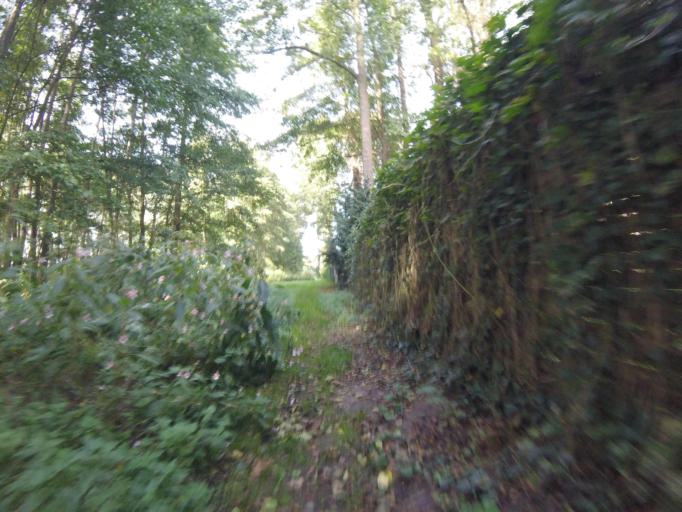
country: DE
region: Brandenburg
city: Bestensee
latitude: 52.2779
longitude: 13.6512
